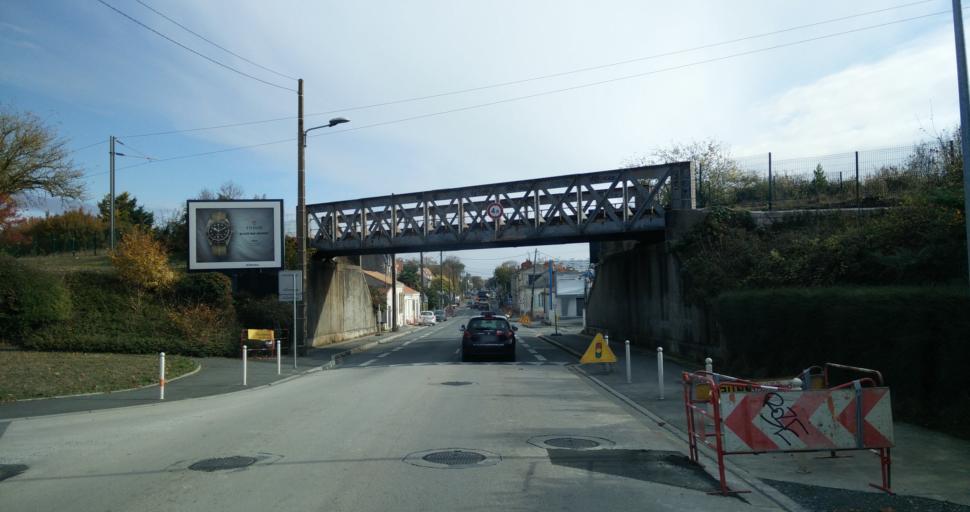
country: FR
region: Poitou-Charentes
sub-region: Departement de la Charente-Maritime
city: La Rochelle
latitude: 46.1637
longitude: -1.1710
